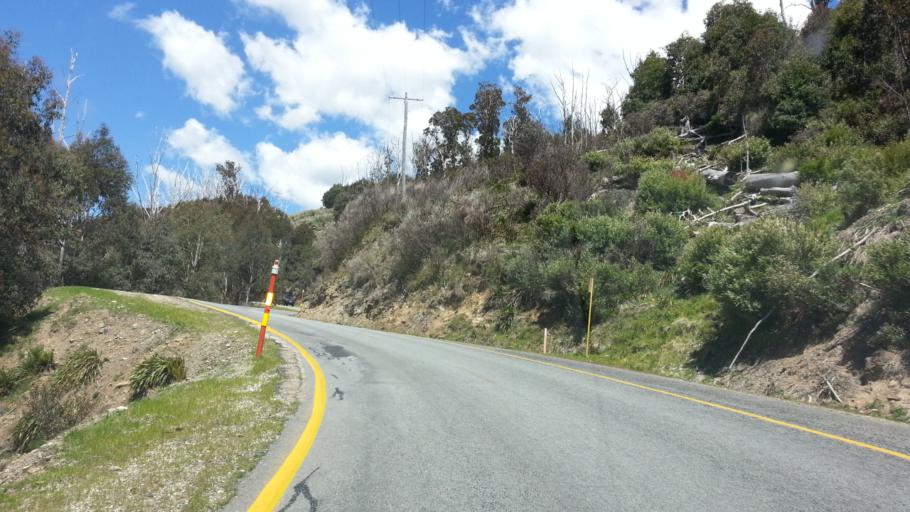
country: AU
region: Victoria
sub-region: Alpine
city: Mount Beauty
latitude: -36.8462
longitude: 147.2666
